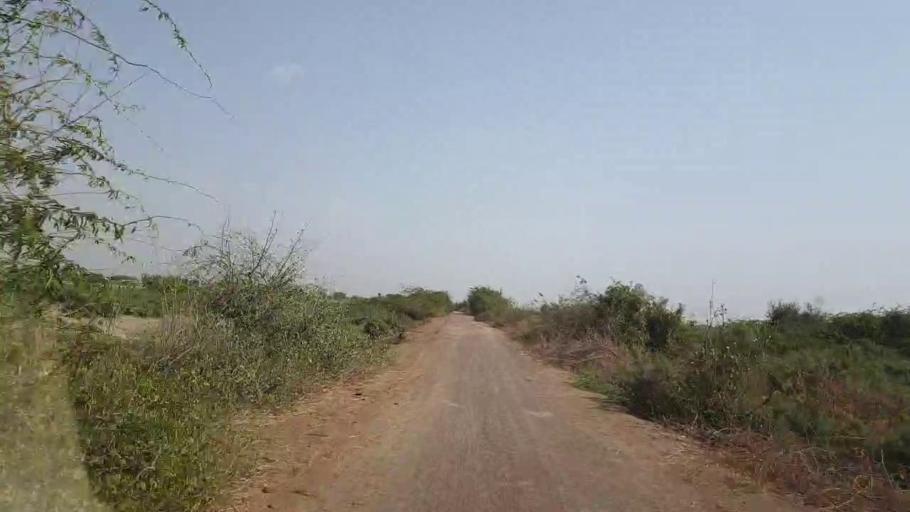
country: PK
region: Sindh
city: Rajo Khanani
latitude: 25.0451
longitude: 68.8499
